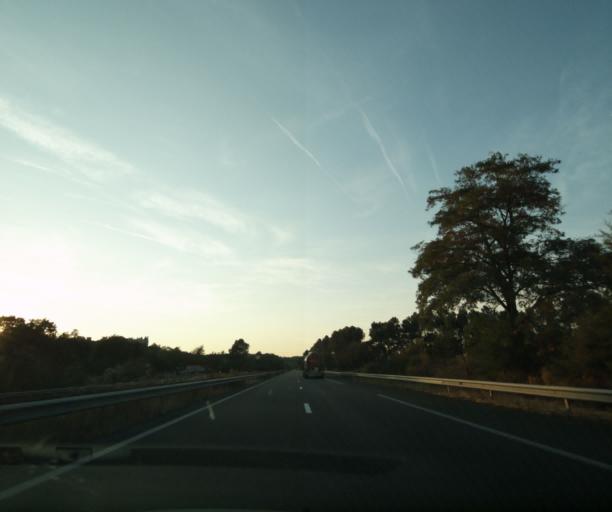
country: FR
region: Aquitaine
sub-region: Departement du Lot-et-Garonne
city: Buzet-sur-Baise
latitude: 44.2488
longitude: 0.3034
